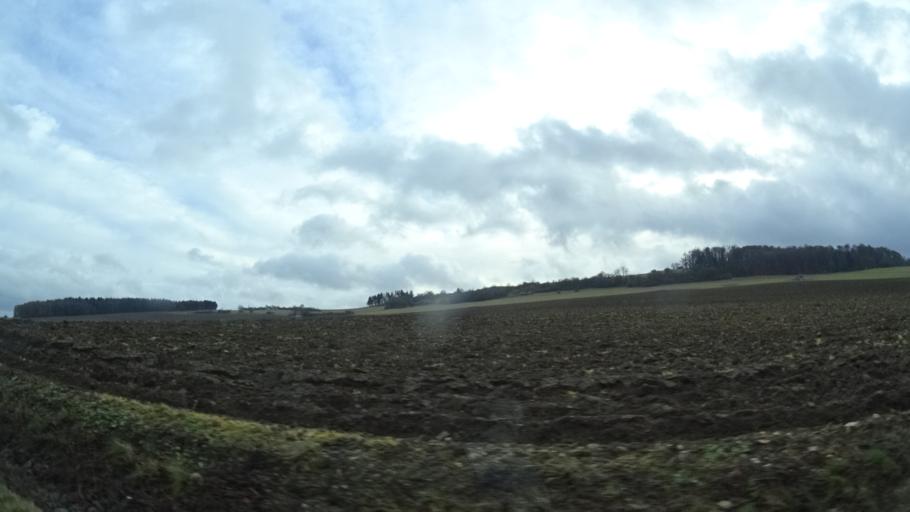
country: DE
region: Thuringia
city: Kaltenwestheim
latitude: 50.6075
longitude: 10.1393
